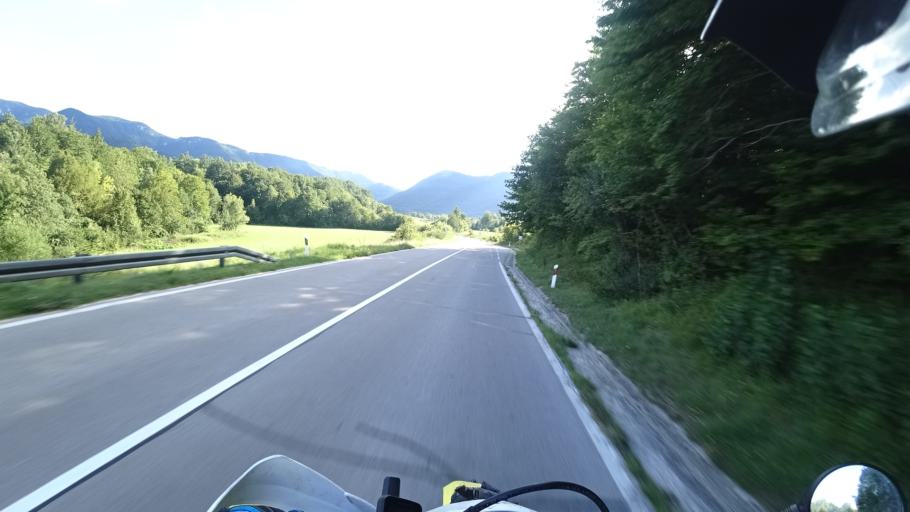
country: HR
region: Zadarska
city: Gracac
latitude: 44.3330
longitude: 16.1131
